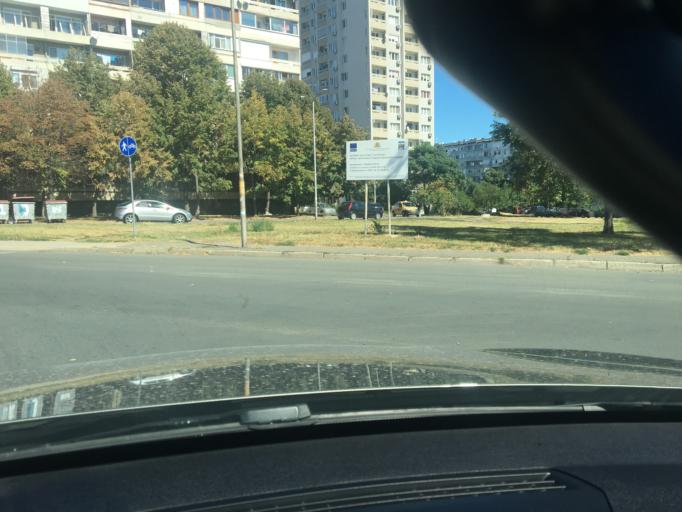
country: BG
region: Burgas
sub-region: Obshtina Burgas
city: Burgas
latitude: 42.5264
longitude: 27.4653
